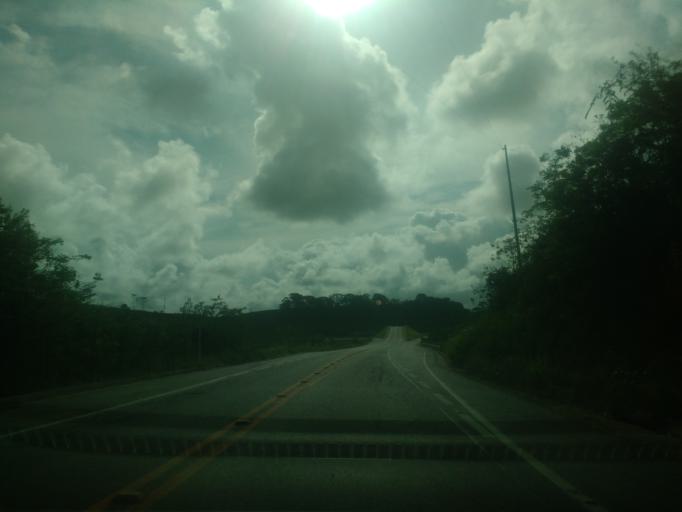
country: BR
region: Alagoas
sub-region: Messias
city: Messias
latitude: -9.3681
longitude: -35.8372
